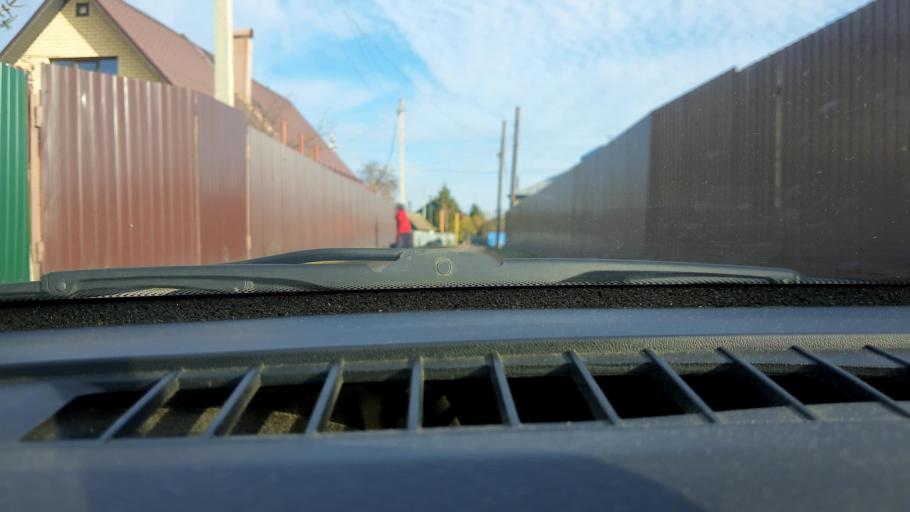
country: RU
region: Nizjnij Novgorod
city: Neklyudovo
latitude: 56.4136
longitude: 43.9764
